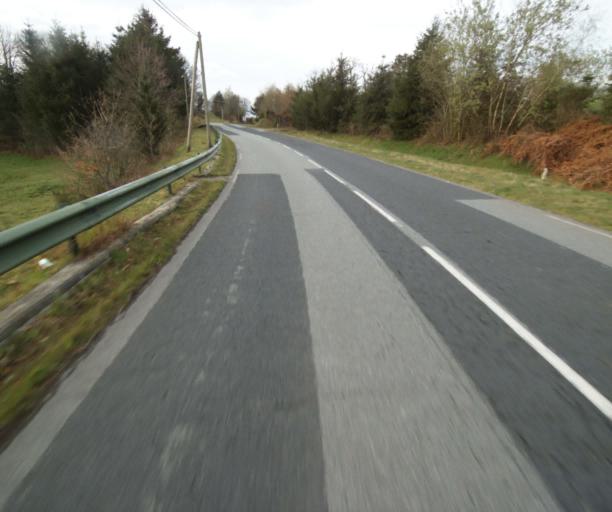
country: FR
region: Limousin
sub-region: Departement de la Correze
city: Correze
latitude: 45.3827
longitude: 1.8644
